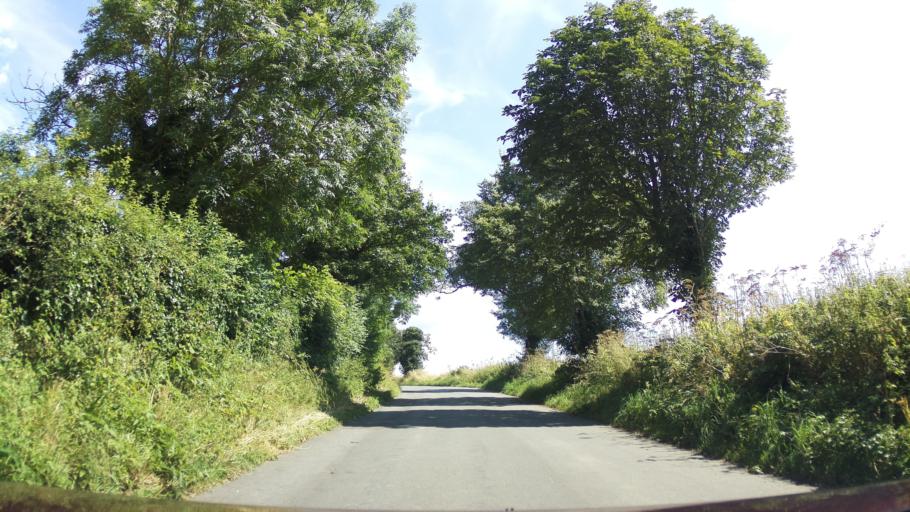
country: GB
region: England
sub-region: West Berkshire
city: Farnborough
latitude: 51.5111
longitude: -1.4025
